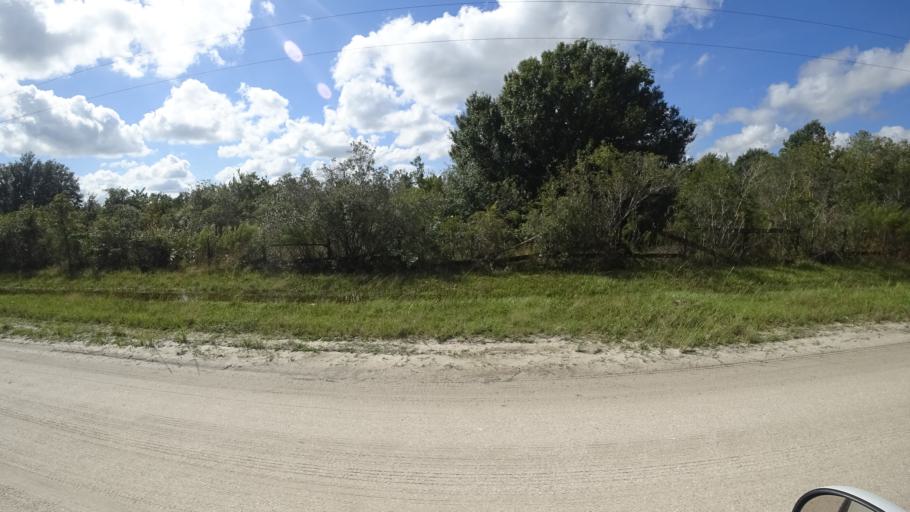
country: US
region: Florida
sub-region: Sarasota County
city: Lake Sarasota
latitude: 27.3662
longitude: -82.1379
